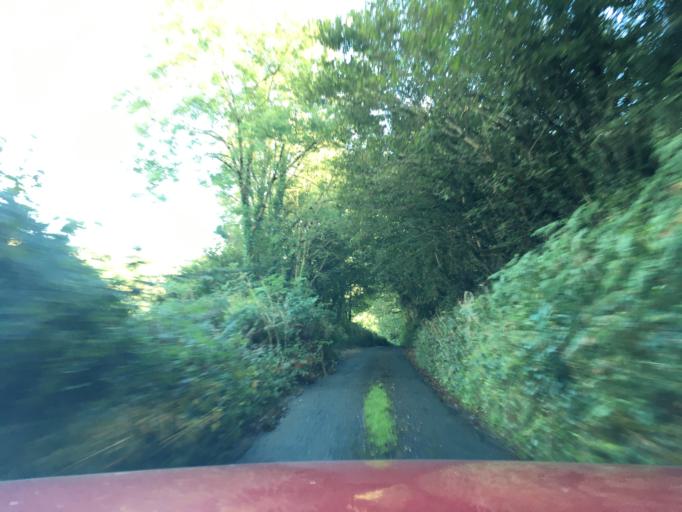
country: GB
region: England
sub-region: Devon
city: Dartmouth
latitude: 50.3388
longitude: -3.6043
